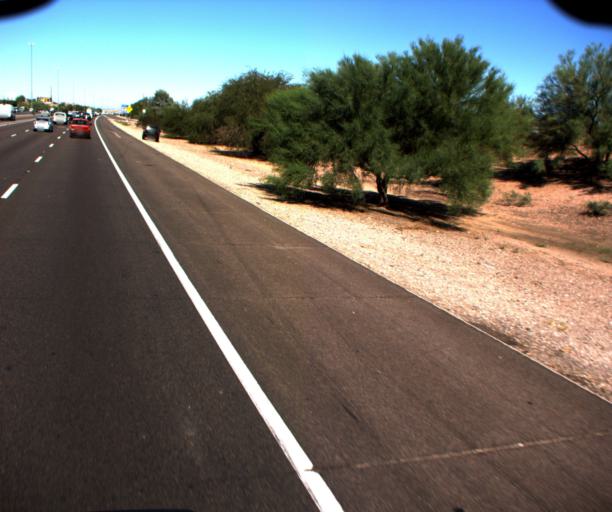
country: US
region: Arizona
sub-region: Maricopa County
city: Guadalupe
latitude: 33.3497
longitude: -111.9716
